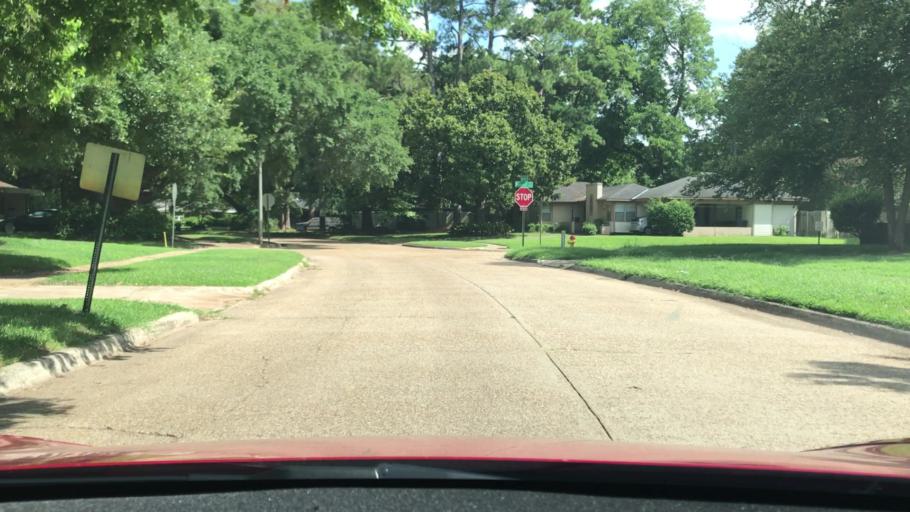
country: US
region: Louisiana
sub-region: Bossier Parish
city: Bossier City
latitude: 32.4615
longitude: -93.7134
